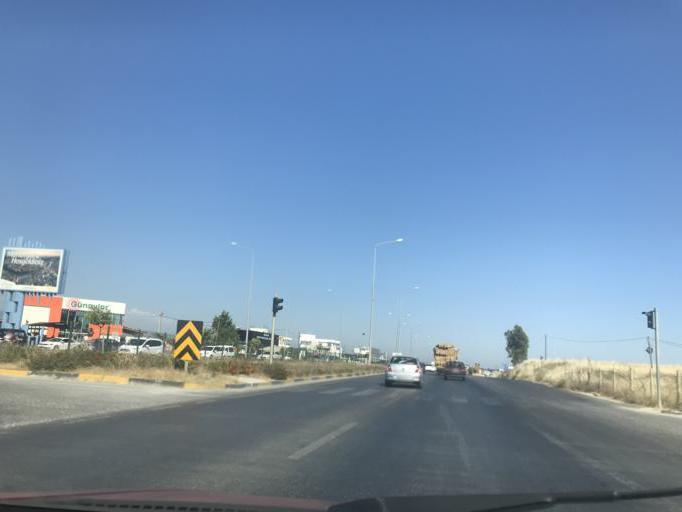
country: TR
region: Antalya
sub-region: Manavgat
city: Side
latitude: 36.8048
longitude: 31.3914
